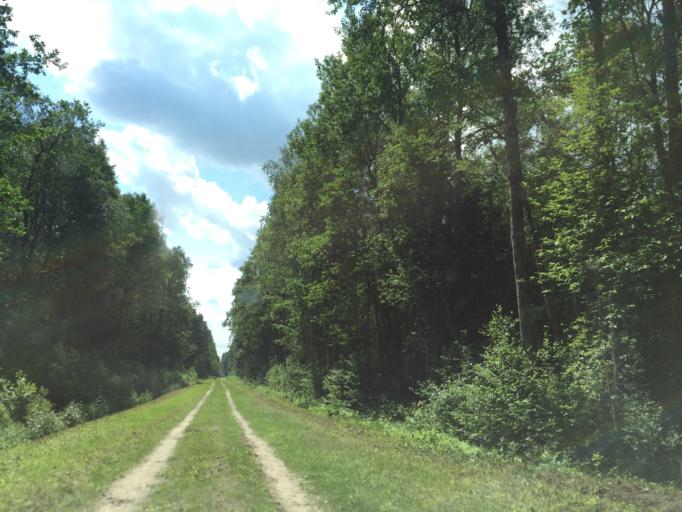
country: LV
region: Ozolnieku
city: Ozolnieki
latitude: 56.6824
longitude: 23.7527
